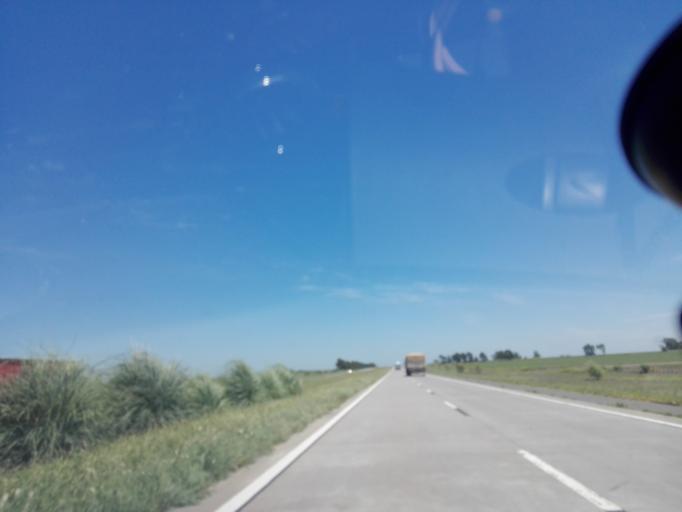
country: AR
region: Santa Fe
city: Armstrong
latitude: -32.7913
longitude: -61.7108
